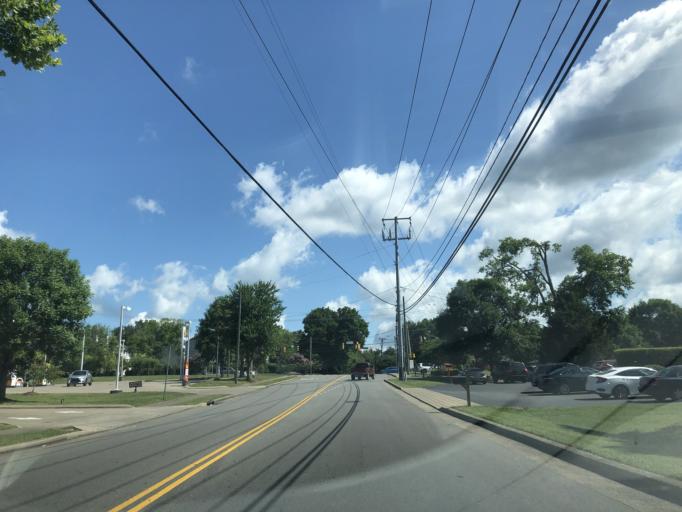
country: US
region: Tennessee
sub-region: Davidson County
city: Belle Meade
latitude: 36.0729
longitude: -86.9264
